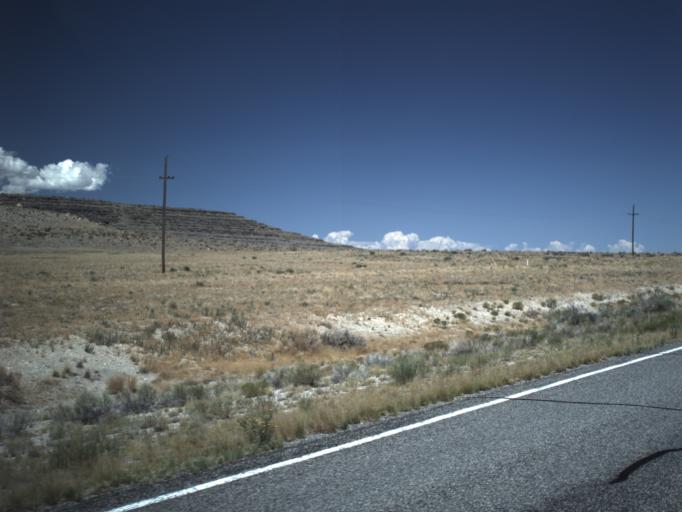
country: US
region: Utah
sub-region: Beaver County
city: Milford
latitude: 39.0442
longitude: -113.2899
